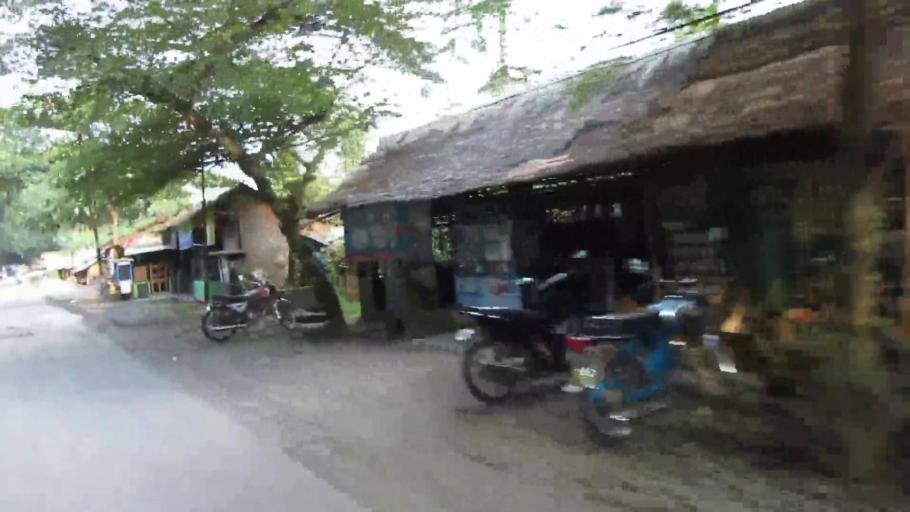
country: ID
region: West Java
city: Balengbeng
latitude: -7.7148
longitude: 108.4836
